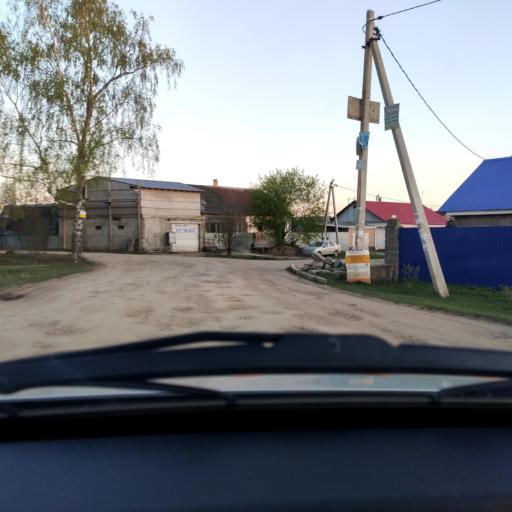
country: RU
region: Bashkortostan
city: Iglino
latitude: 54.7452
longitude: 56.2782
